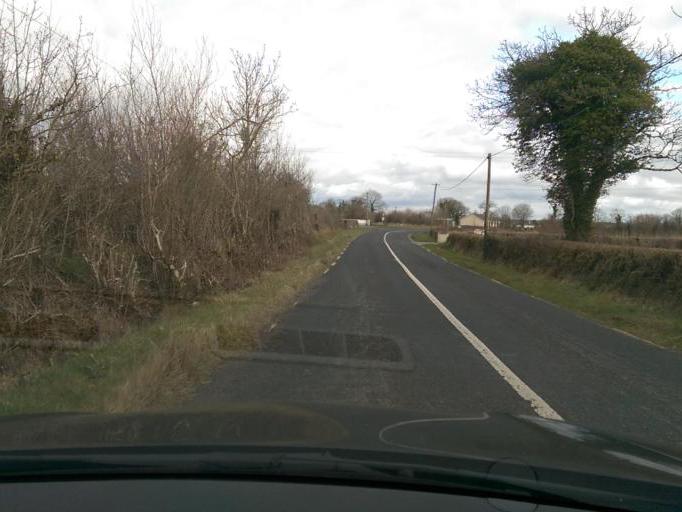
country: IE
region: Connaught
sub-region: County Galway
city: Ballinasloe
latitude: 53.3322
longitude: -8.3367
